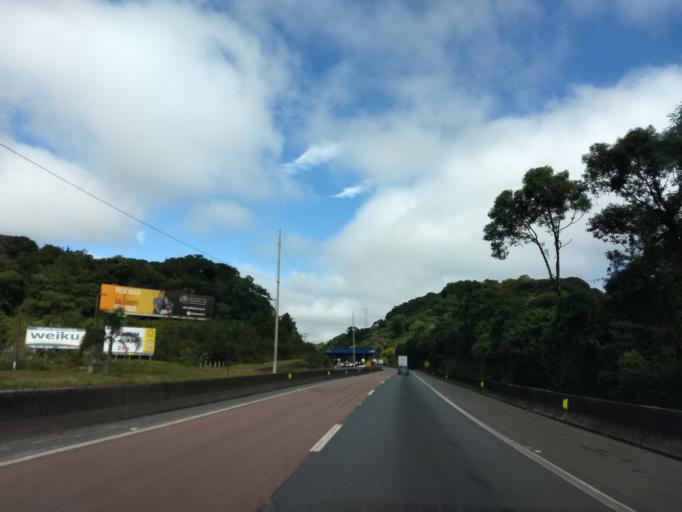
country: BR
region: Parana
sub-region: Sao Jose Dos Pinhais
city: Sao Jose dos Pinhais
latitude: -25.8526
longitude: -48.9741
